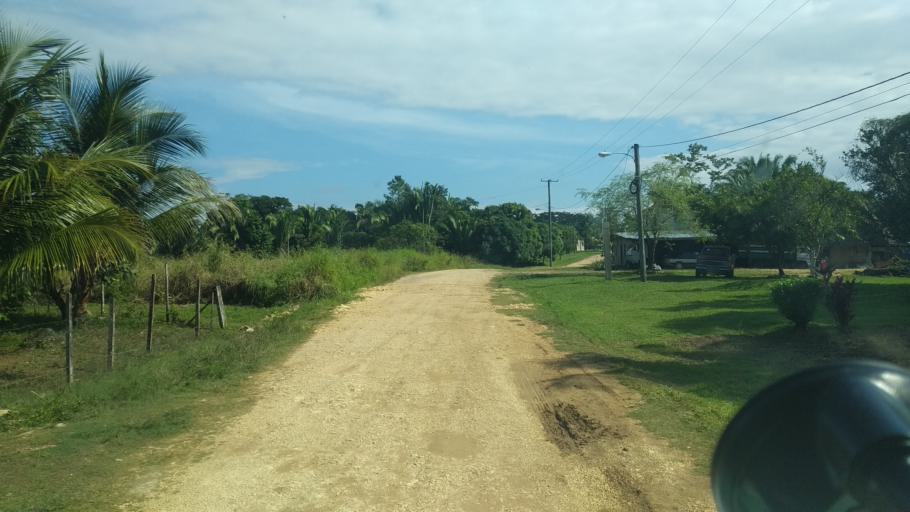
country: BZ
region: Toledo
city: Punta Gorda
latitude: 16.2147
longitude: -88.9087
